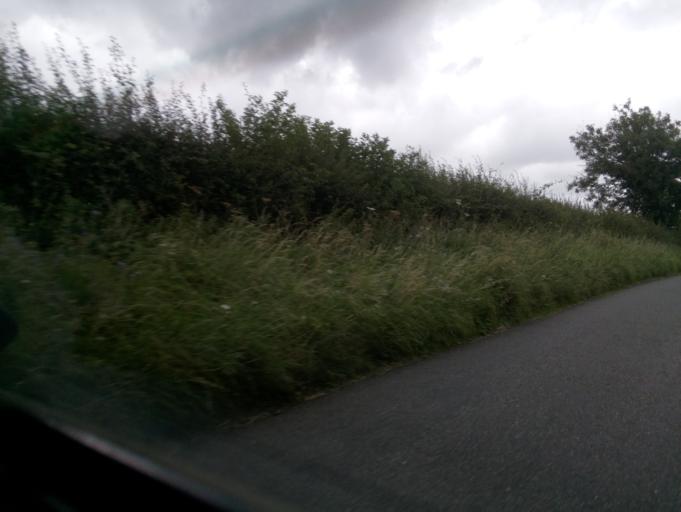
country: GB
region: England
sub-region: Gloucestershire
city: Chalford
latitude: 51.7872
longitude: -2.1123
